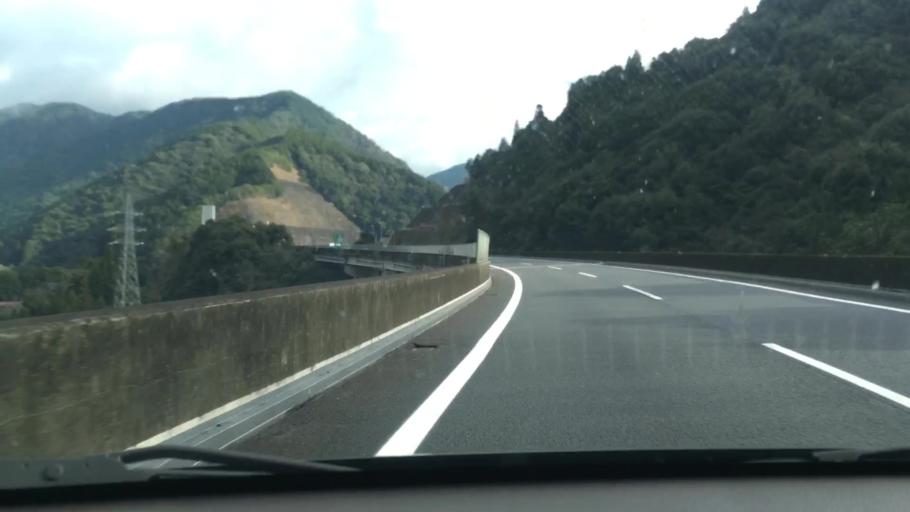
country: JP
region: Kumamoto
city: Yatsushiro
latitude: 32.4442
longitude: 130.6645
